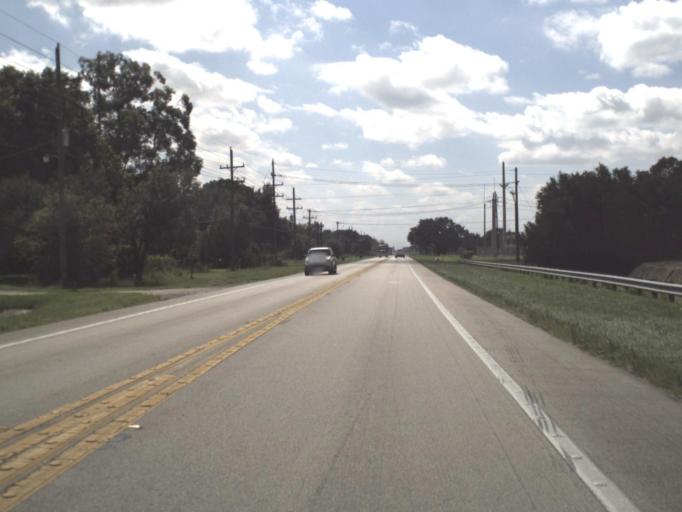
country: US
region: Florida
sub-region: Hendry County
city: LaBelle
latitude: 26.7058
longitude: -81.4373
